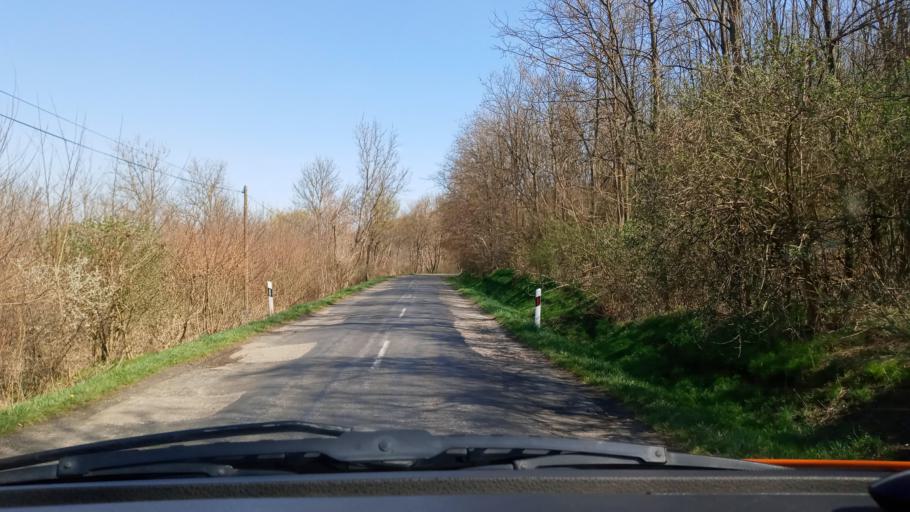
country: HU
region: Baranya
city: Boly
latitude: 46.0500
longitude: 18.4545
